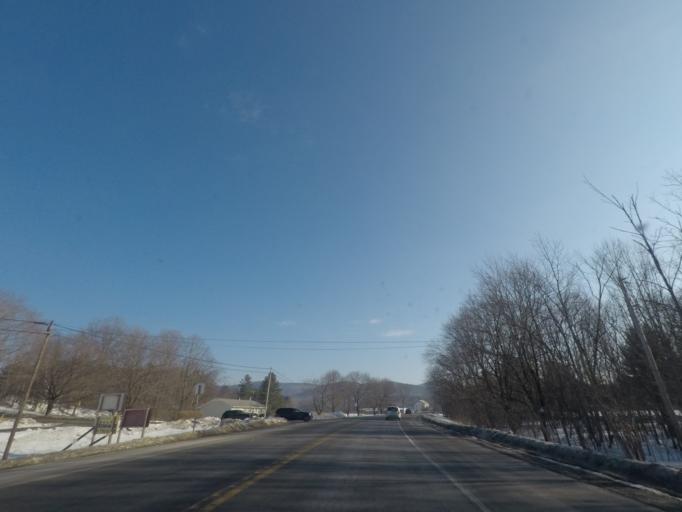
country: US
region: Massachusetts
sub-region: Berkshire County
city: Lanesborough
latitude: 42.5428
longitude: -73.3618
